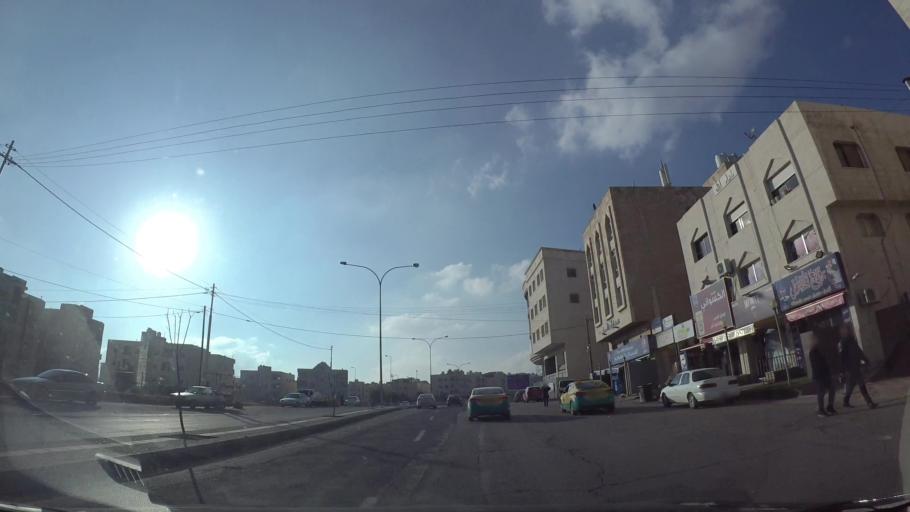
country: JO
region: Amman
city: Amman
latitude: 31.9798
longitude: 35.9414
